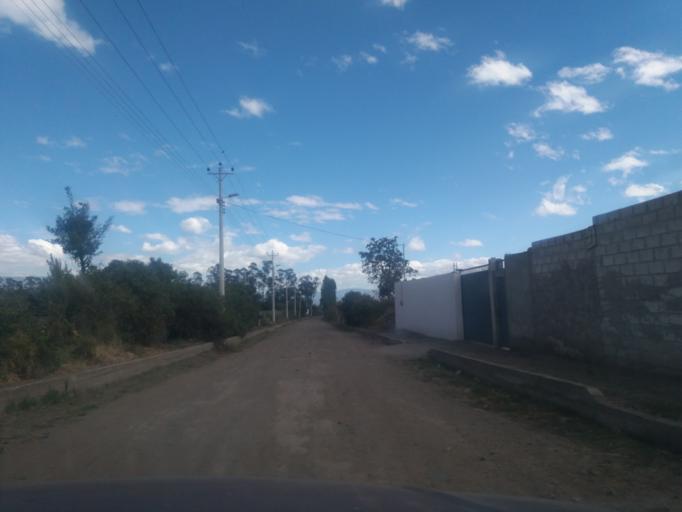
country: EC
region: Pichincha
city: Sangolqui
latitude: -0.1793
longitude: -78.3370
